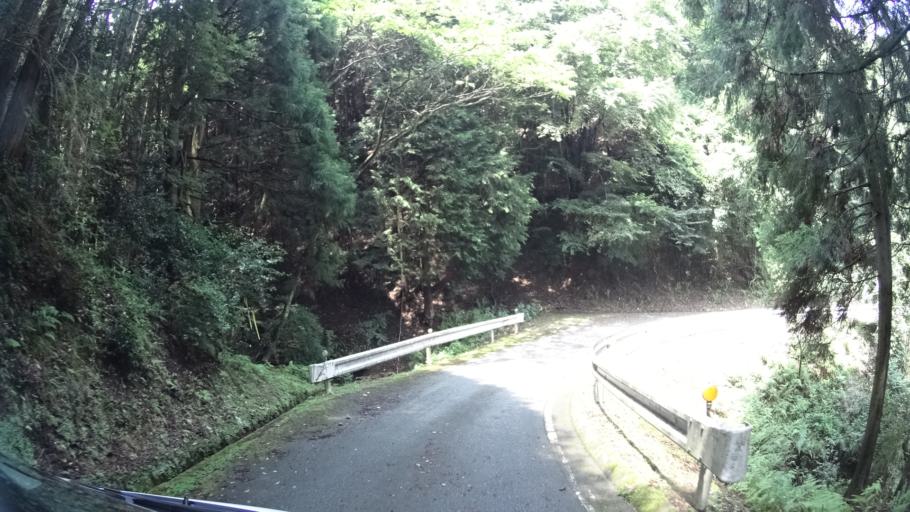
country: JP
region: Hyogo
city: Sasayama
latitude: 35.1713
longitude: 135.1995
